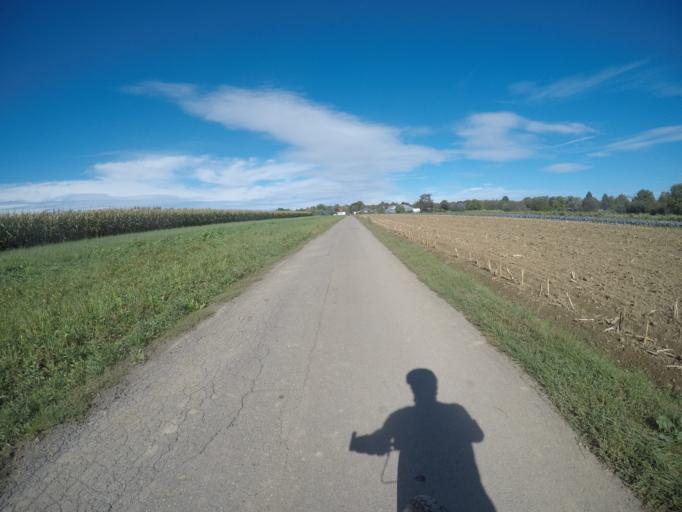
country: DE
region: Baden-Wuerttemberg
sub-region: Regierungsbezirk Stuttgart
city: Leinfelden-Echterdingen
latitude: 48.7353
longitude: 9.1575
